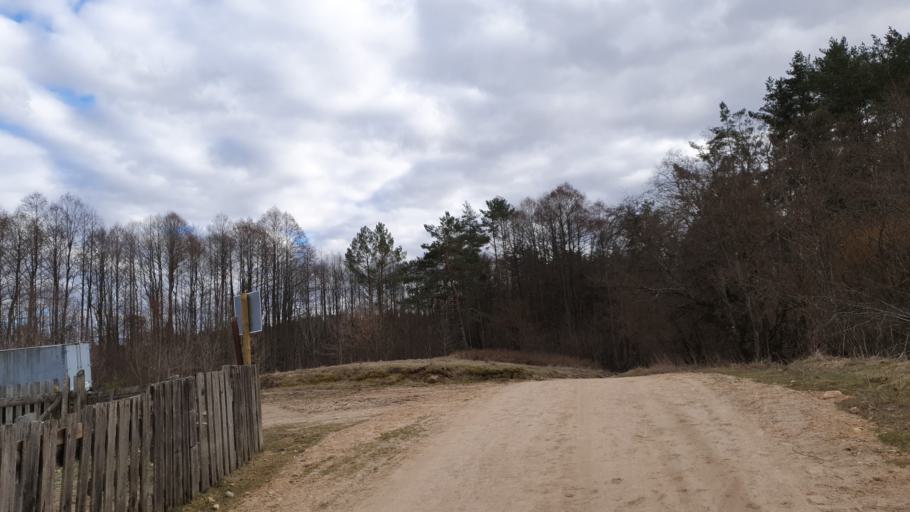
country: LT
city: Grigiskes
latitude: 54.7333
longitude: 25.0278
